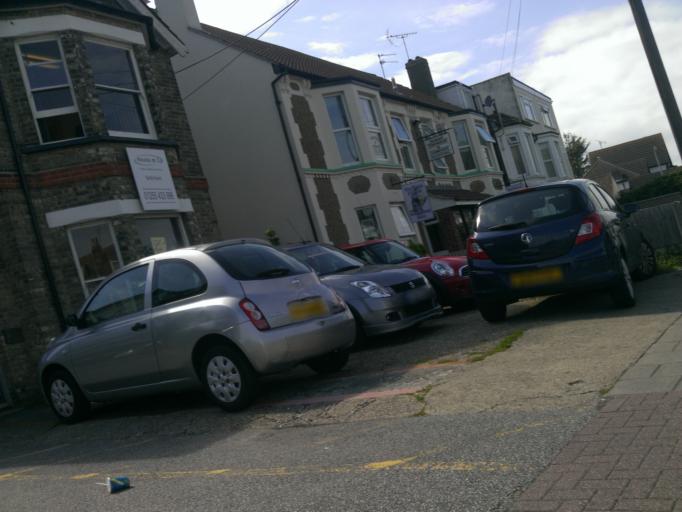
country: GB
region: England
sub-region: Essex
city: Clacton-on-Sea
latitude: 51.7902
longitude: 1.1505
